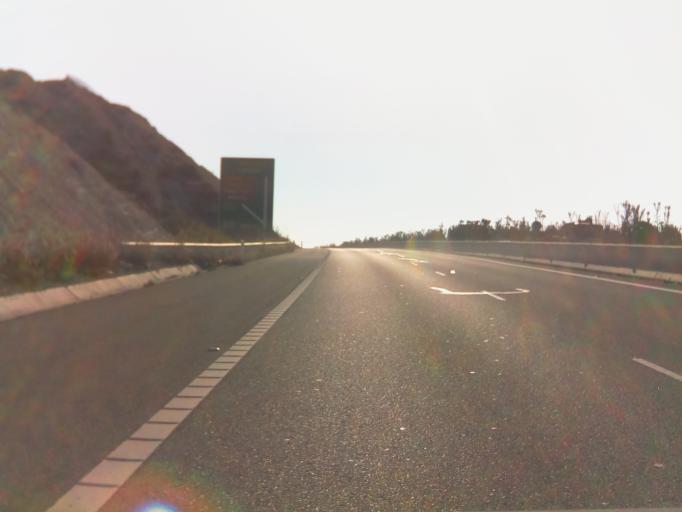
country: CY
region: Limassol
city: Pissouri
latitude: 34.6779
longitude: 32.6030
